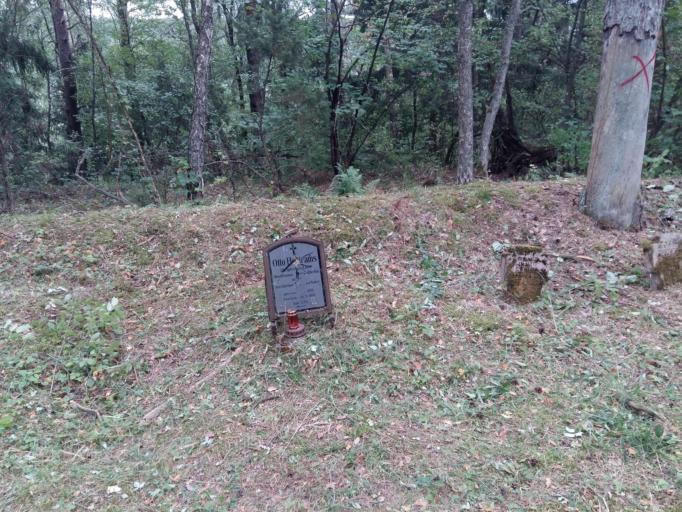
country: LT
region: Alytaus apskritis
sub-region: Alytaus rajonas
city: Daugai
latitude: 54.1632
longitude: 24.2007
